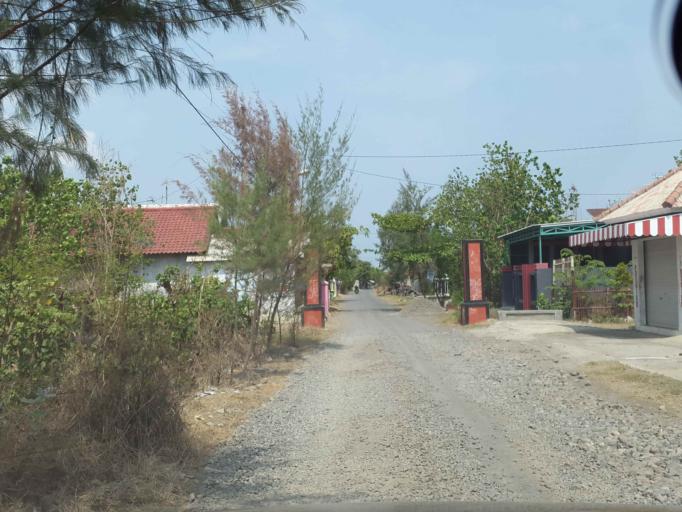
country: ID
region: Central Java
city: Dukuhturi
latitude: -6.8405
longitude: 109.0655
